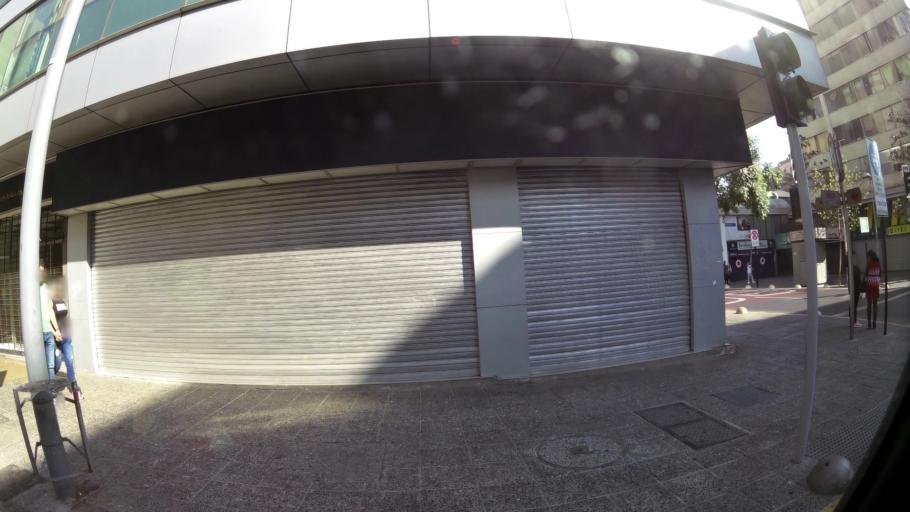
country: CL
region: Santiago Metropolitan
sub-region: Provincia de Santiago
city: Santiago
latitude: -33.4371
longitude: -70.6484
